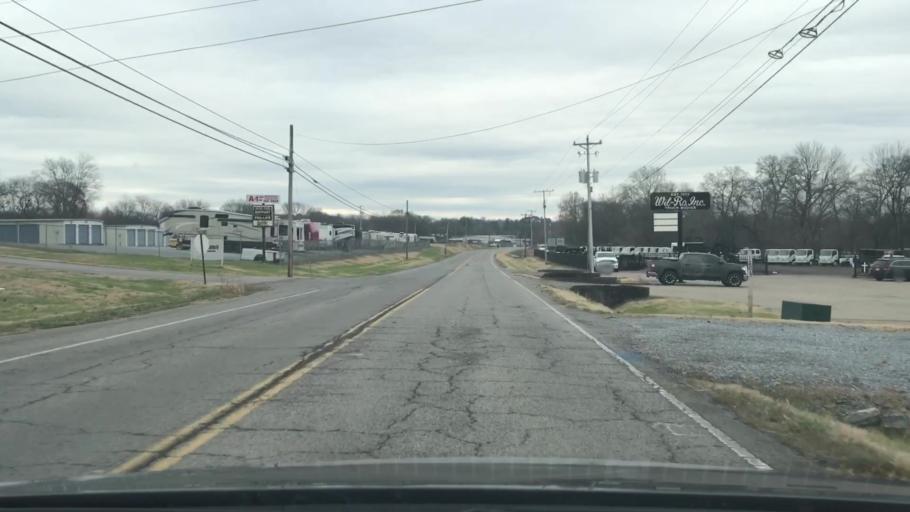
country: US
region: Tennessee
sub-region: Sumner County
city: Gallatin
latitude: 36.4172
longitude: -86.4554
